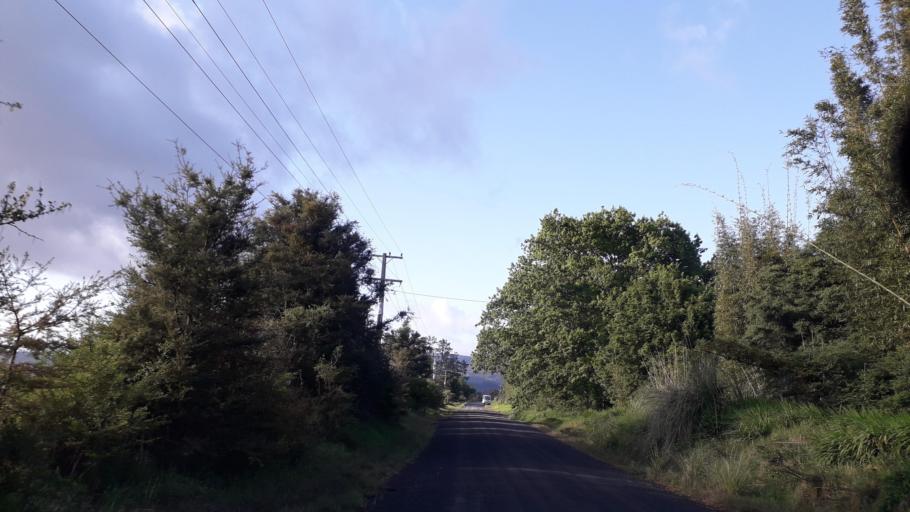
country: NZ
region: Northland
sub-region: Far North District
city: Waimate North
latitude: -35.4968
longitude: 173.6992
